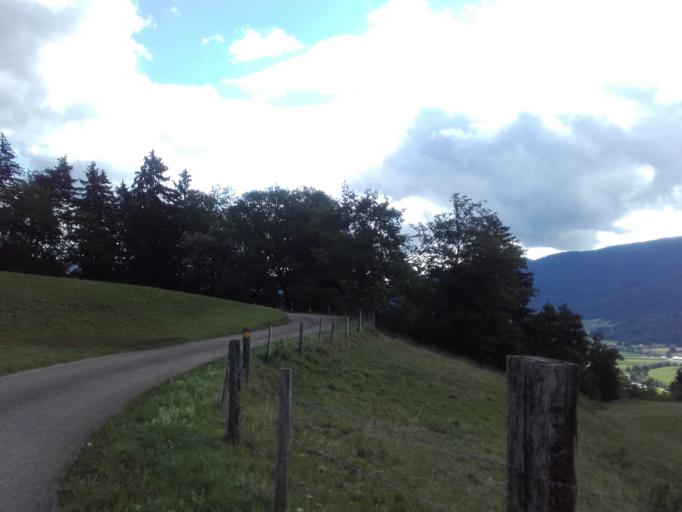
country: CH
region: Solothurn
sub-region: Bezirk Thal
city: Matzendorf
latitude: 47.3096
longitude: 7.5885
